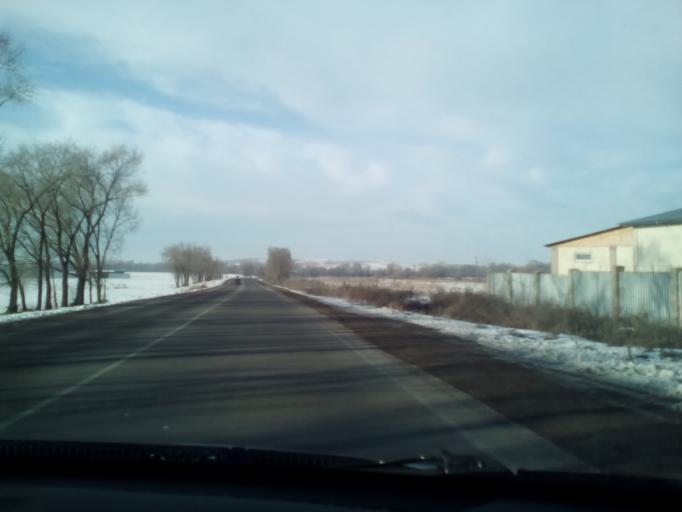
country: KZ
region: Almaty Oblysy
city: Burunday
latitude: 43.2148
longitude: 76.4147
